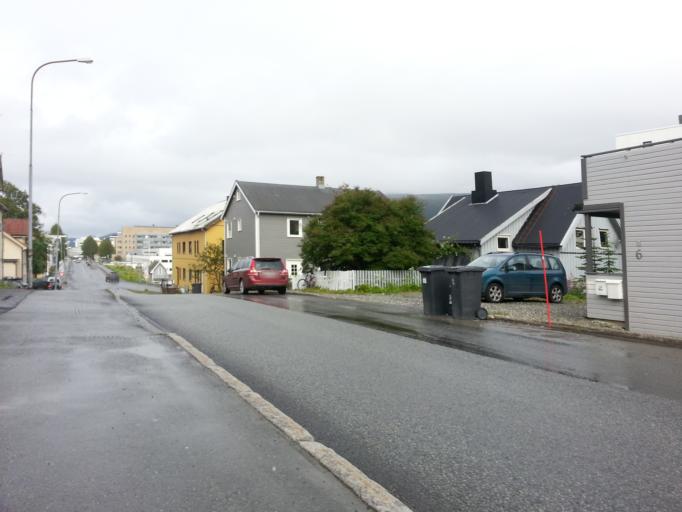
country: NO
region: Troms
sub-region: Tromso
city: Tromso
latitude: 69.6418
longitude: 18.9401
